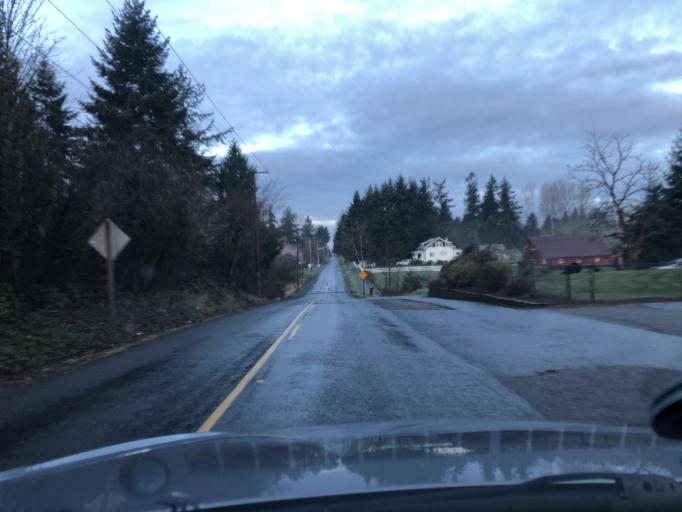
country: US
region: Washington
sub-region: Pierce County
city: North Puyallup
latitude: 47.2249
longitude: -122.2801
